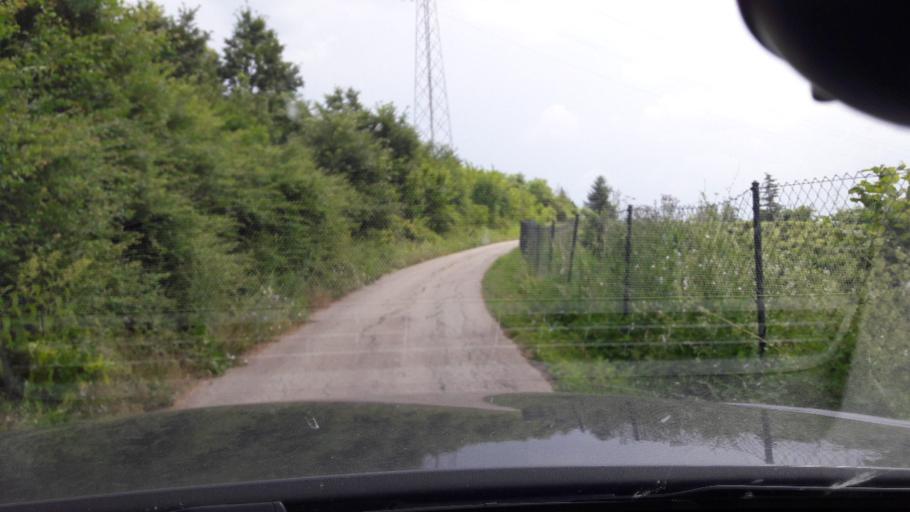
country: RS
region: Central Serbia
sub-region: Belgrade
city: Sopot
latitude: 44.6151
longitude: 20.5895
